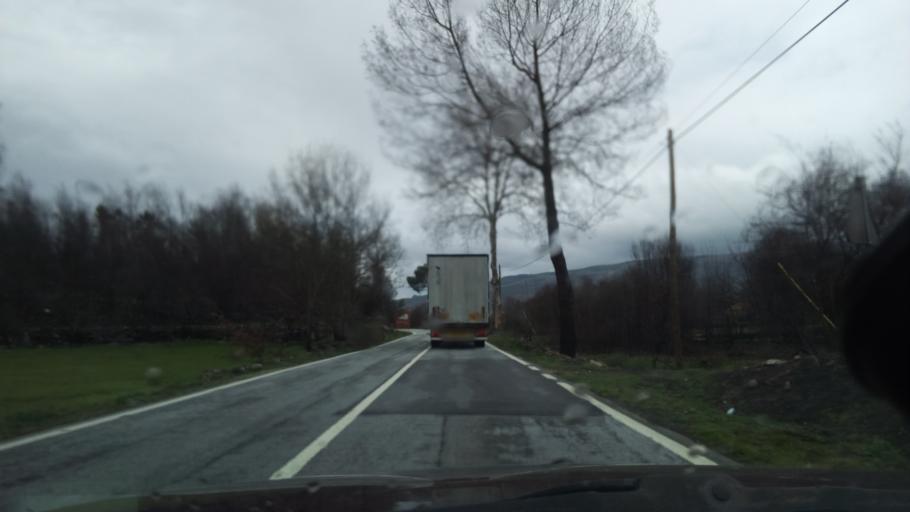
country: PT
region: Guarda
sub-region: Fornos de Algodres
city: Fornos de Algodres
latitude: 40.5560
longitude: -7.4989
